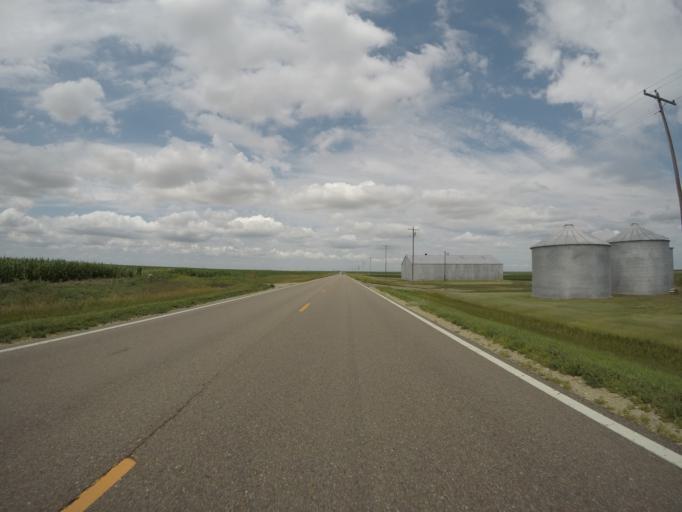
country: US
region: Kansas
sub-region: Rawlins County
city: Atwood
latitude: 39.6639
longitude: -101.0567
